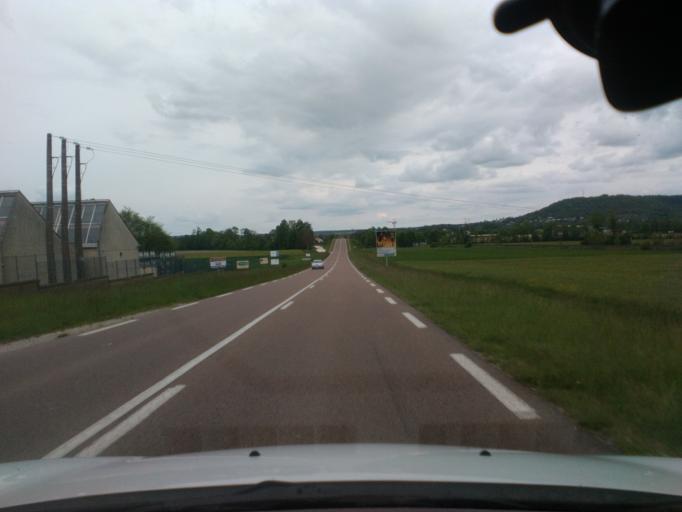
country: FR
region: Champagne-Ardenne
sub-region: Departement de l'Aube
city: Bar-sur-Aube
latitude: 48.2489
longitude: 4.6887
